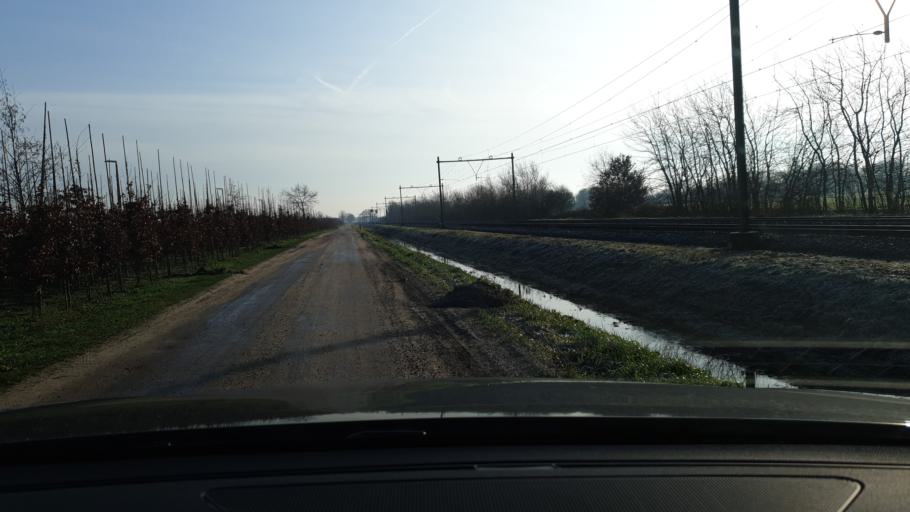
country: NL
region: Limburg
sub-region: Gemeente Peel en Maas
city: Maasbree
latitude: 51.4218
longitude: 6.0524
